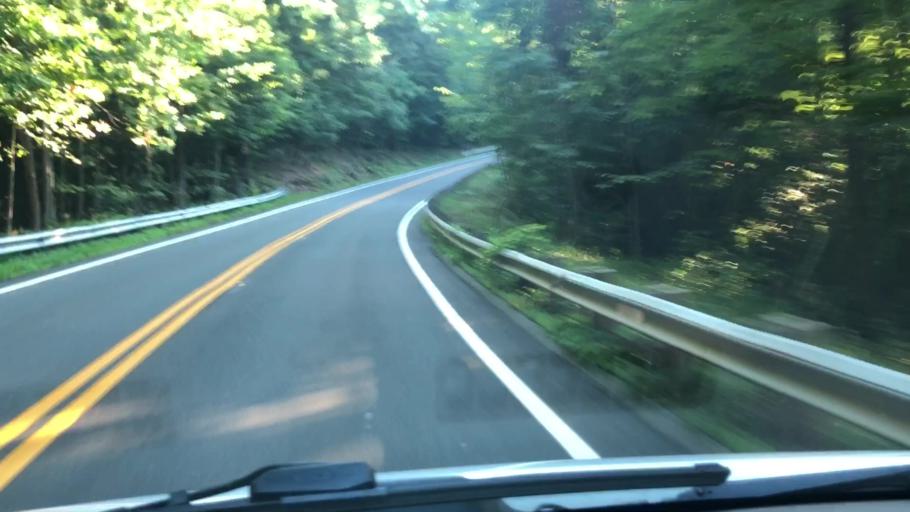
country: US
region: Massachusetts
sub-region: Hampshire County
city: Westhampton
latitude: 42.2990
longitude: -72.8680
